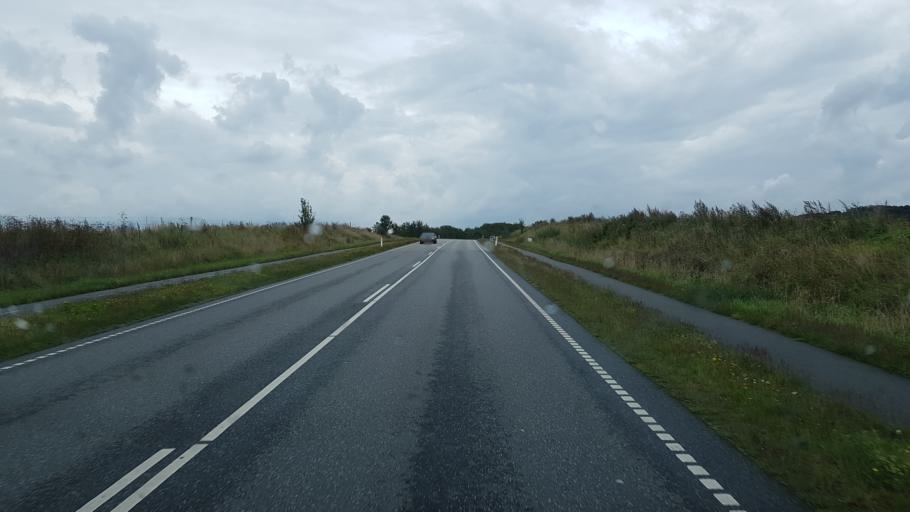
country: DK
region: Central Jutland
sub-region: Horsens Kommune
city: Horsens
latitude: 55.9045
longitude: 9.7400
